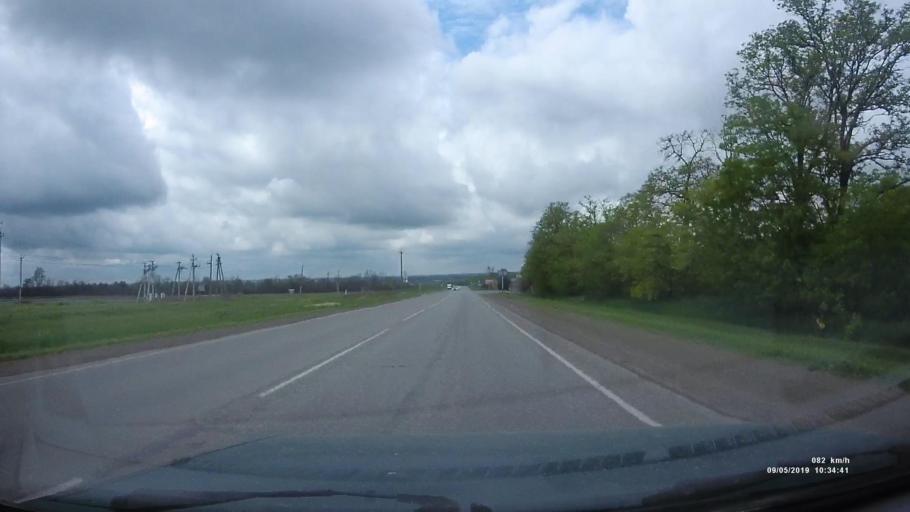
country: RU
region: Rostov
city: Peshkovo
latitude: 47.0515
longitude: 39.4181
